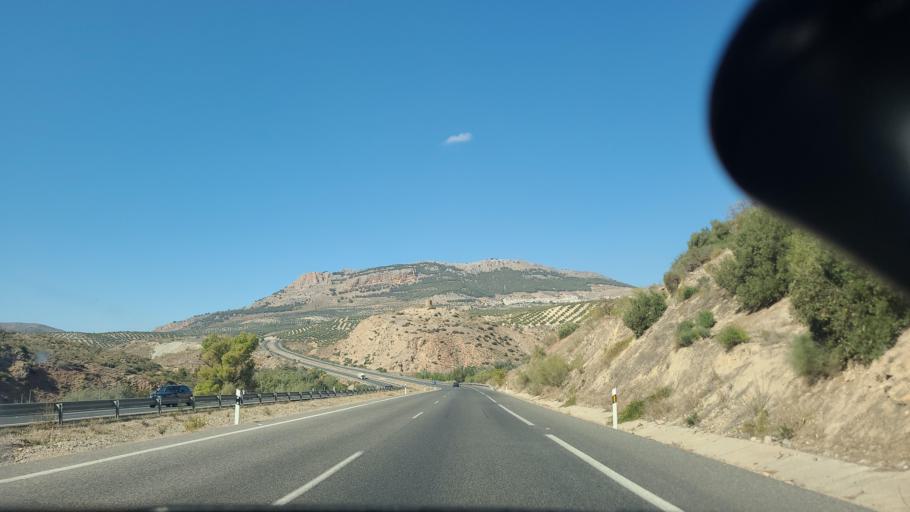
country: ES
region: Andalusia
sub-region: Provincia de Jaen
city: Pegalajar
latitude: 37.7068
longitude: -3.6379
